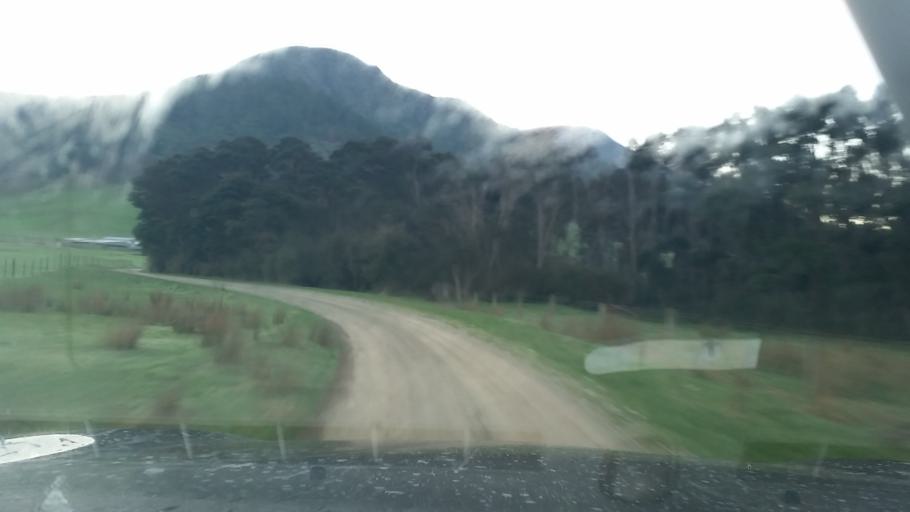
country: NZ
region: Marlborough
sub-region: Marlborough District
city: Picton
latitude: -41.1578
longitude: 174.1327
